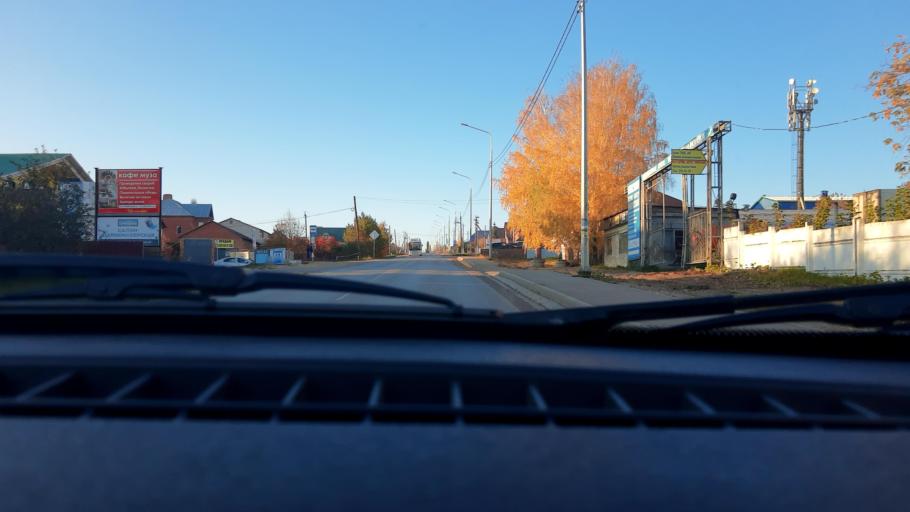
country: RU
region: Bashkortostan
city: Mikhaylovka
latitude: 54.8086
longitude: 55.8886
